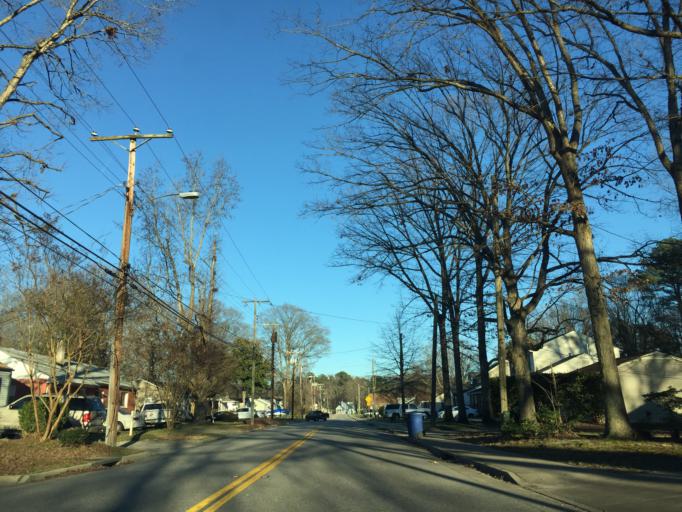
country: US
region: Virginia
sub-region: City of Newport News
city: Newport News
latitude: 37.0789
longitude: -76.5002
